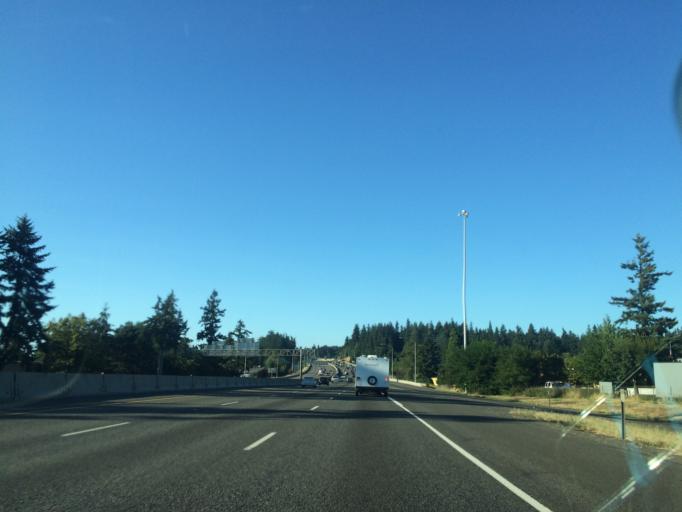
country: US
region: Oregon
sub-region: Washington County
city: Durham
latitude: 45.3978
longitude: -122.7465
